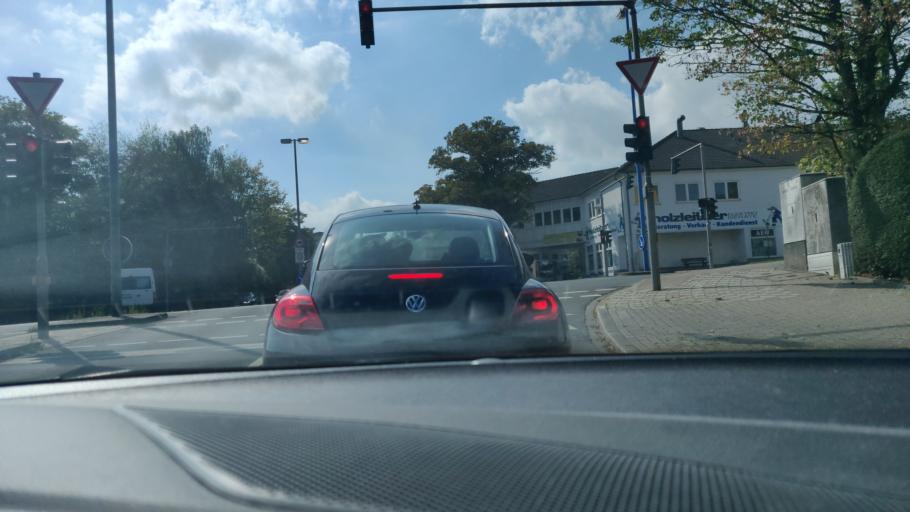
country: DE
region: North Rhine-Westphalia
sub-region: Regierungsbezirk Dusseldorf
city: Velbert
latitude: 51.3324
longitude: 7.0330
